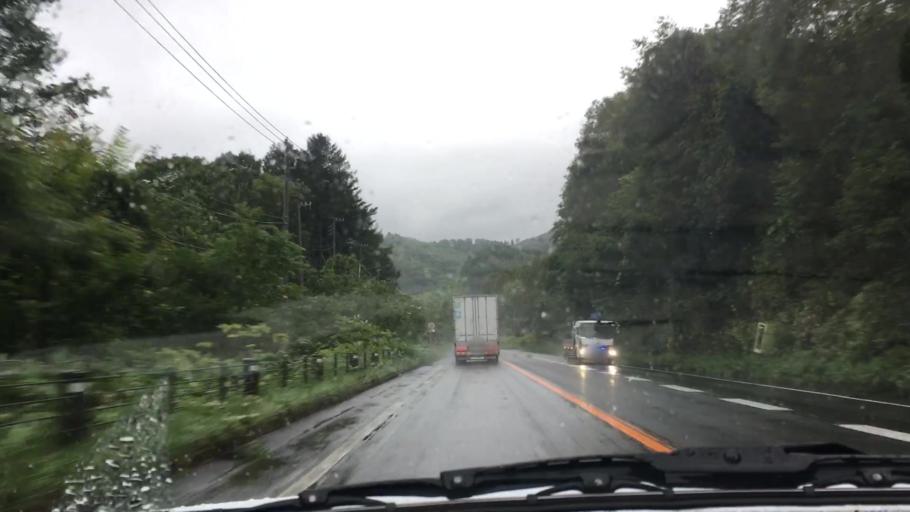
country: JP
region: Hokkaido
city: Niseko Town
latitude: 42.5991
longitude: 140.6650
